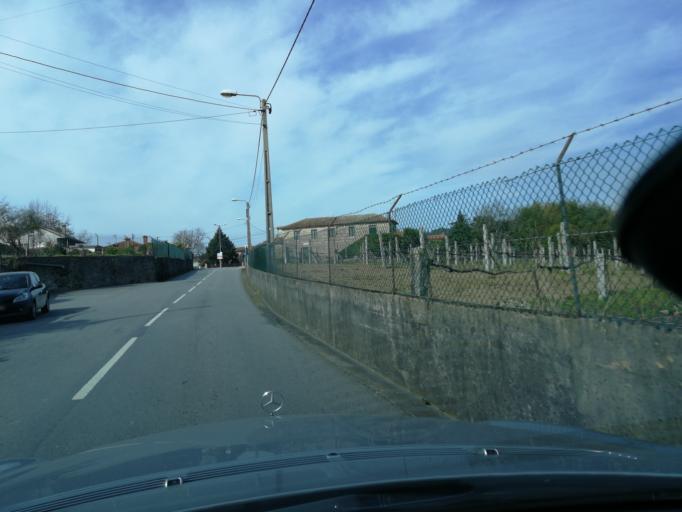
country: PT
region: Braga
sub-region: Vila Nova de Famalicao
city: Vila Nova de Famalicao
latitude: 41.4337
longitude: -8.5220
